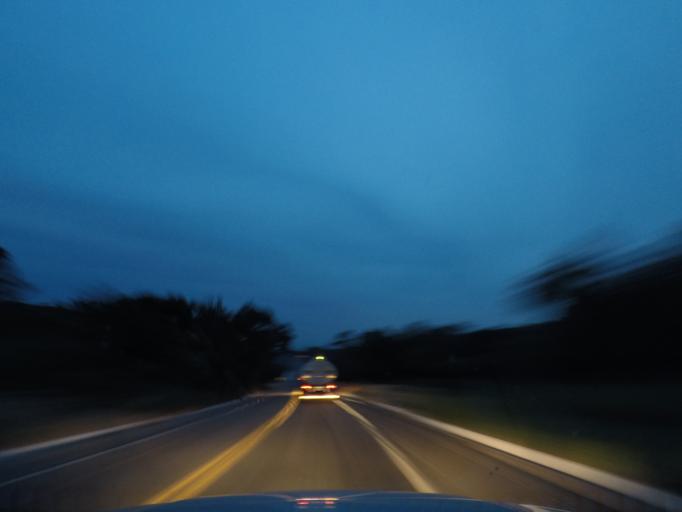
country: BR
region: Bahia
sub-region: Andarai
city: Vera Cruz
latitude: -12.4929
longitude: -41.3280
